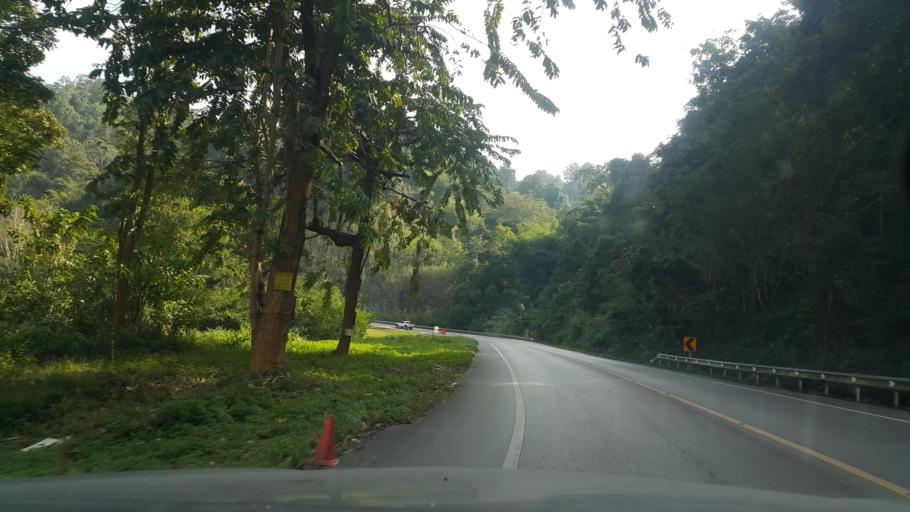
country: TH
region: Lampang
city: Wang Nuea
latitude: 19.0648
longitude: 99.7282
